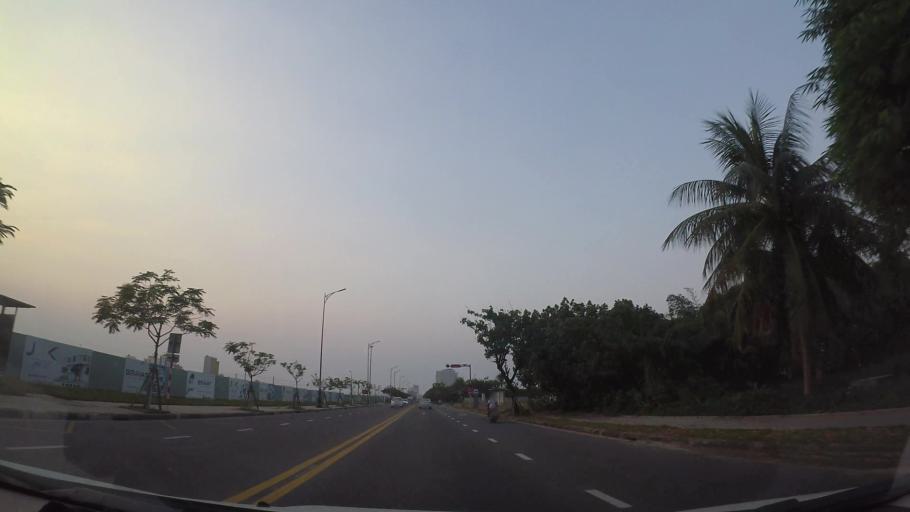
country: VN
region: Da Nang
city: Ngu Hanh Son
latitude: 16.0147
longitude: 108.2613
